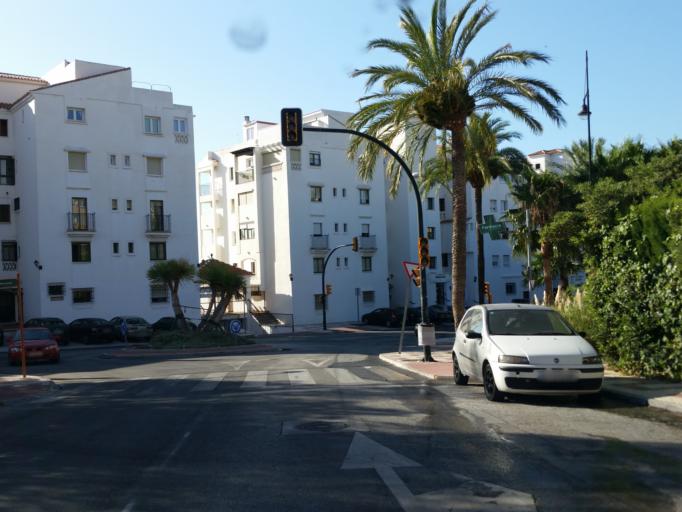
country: ES
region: Andalusia
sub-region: Provincia de Malaga
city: Torremolinos
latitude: 36.6037
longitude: -4.5291
